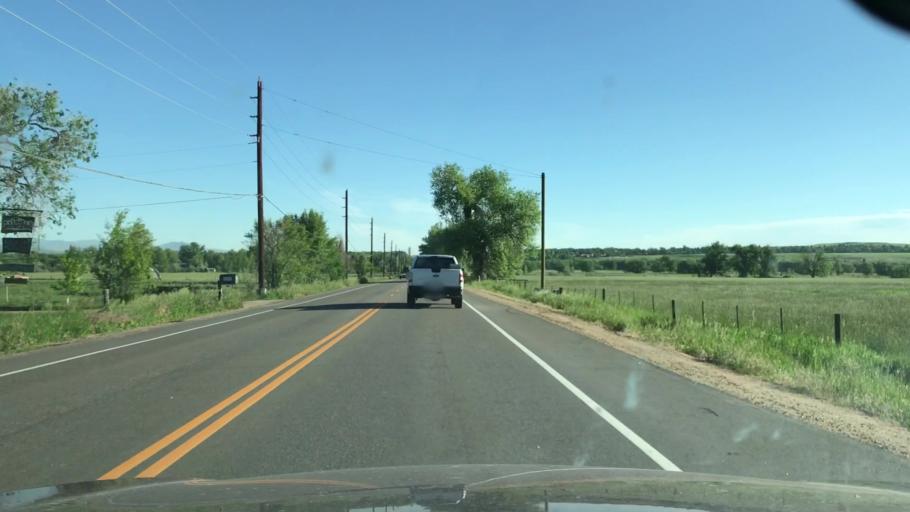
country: US
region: Colorado
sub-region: Boulder County
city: Gunbarrel
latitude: 40.0356
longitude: -105.1784
